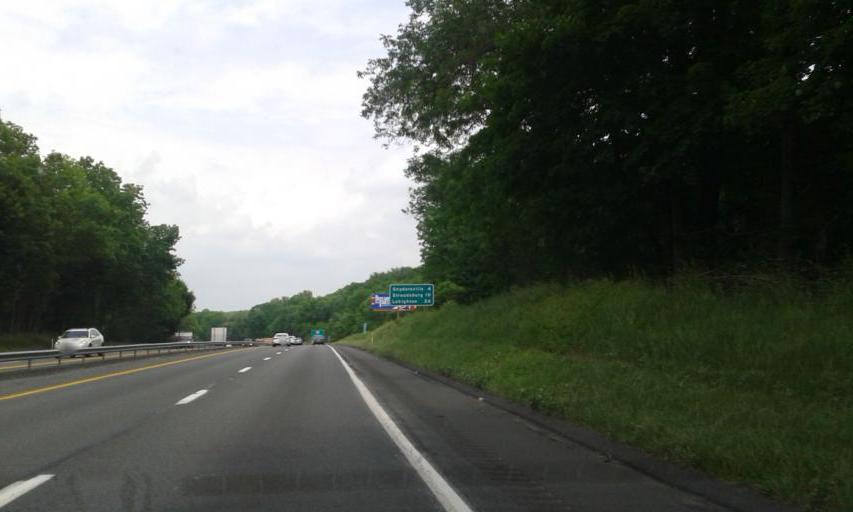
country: US
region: Pennsylvania
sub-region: Monroe County
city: Saylorsburg
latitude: 40.8988
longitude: -75.3084
